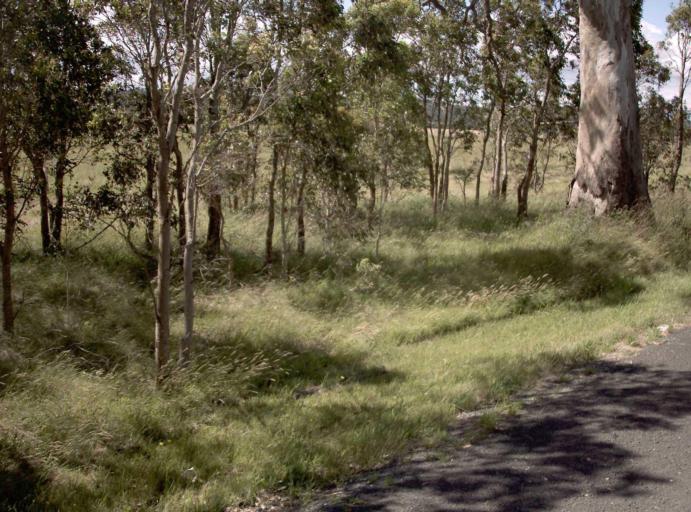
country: AU
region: Victoria
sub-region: Latrobe
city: Traralgon
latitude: -38.1433
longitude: 146.5269
